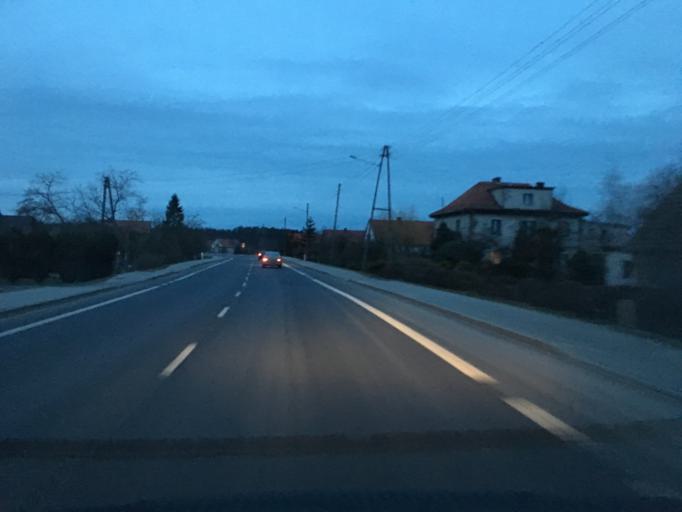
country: PL
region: Opole Voivodeship
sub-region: Powiat opolski
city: Dabrowa
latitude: 50.7240
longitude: 17.7536
